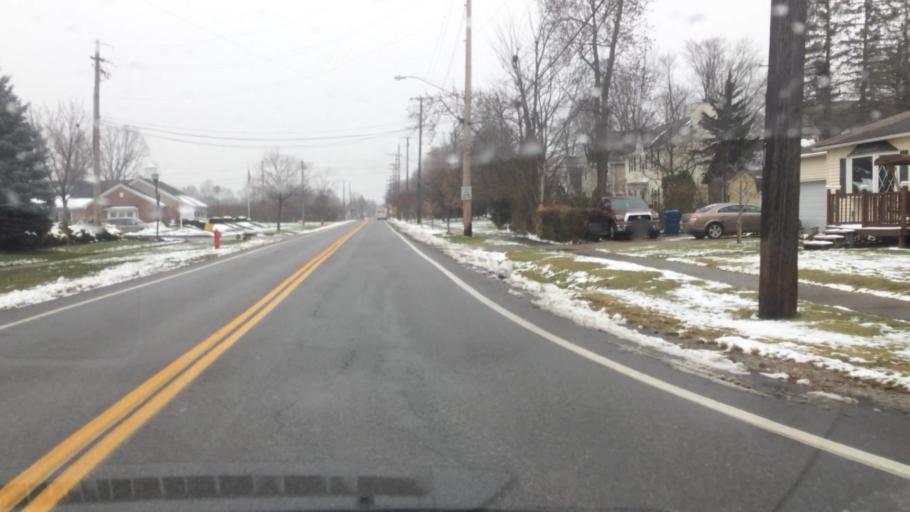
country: US
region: Ohio
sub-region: Cuyahoga County
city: Olmsted Falls
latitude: 41.3728
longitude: -81.9095
